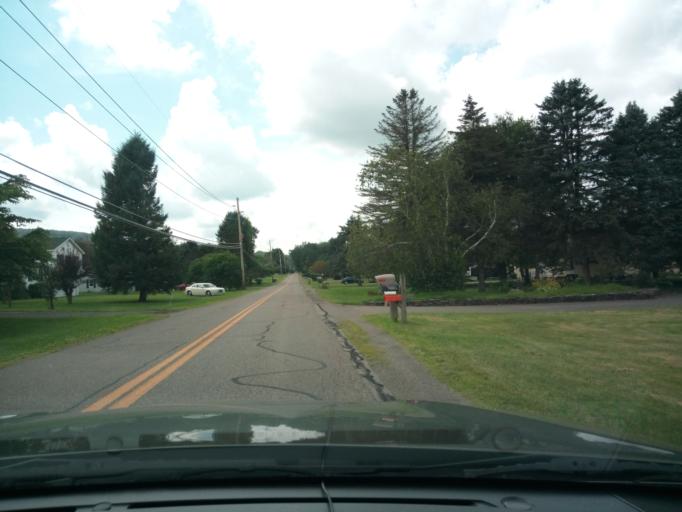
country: US
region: Pennsylvania
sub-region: Bradford County
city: South Waverly
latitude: 41.9960
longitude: -76.5727
